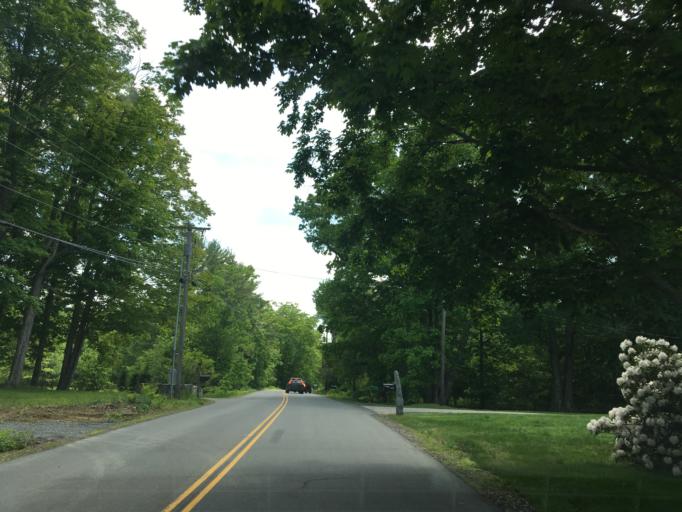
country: US
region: New Hampshire
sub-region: Rockingham County
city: Greenland
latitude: 43.0298
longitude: -70.8527
